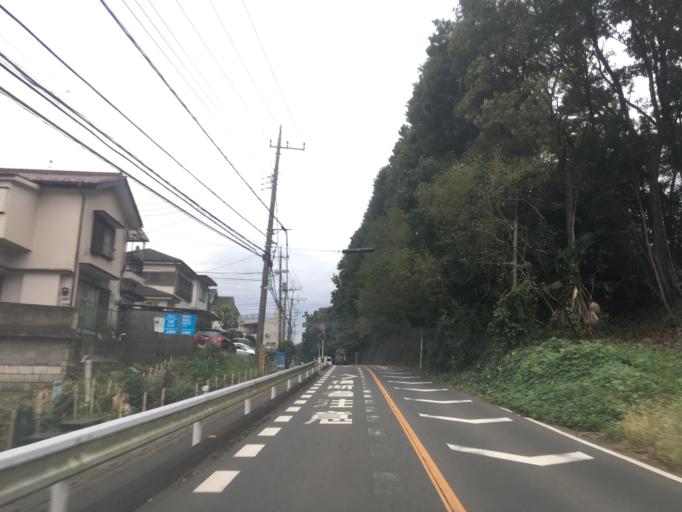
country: JP
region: Tokyo
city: Higashimurayama-shi
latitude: 35.7741
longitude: 139.4519
